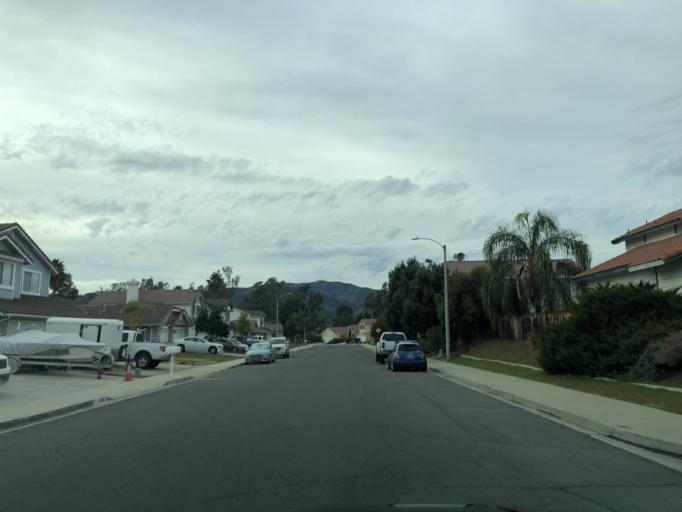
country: US
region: California
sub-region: Riverside County
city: Wildomar
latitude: 33.6051
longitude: -117.2639
